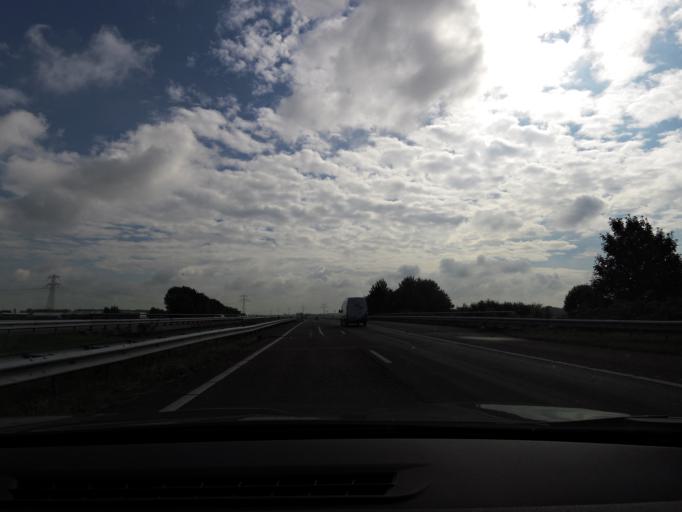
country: NL
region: Zeeland
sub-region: Gemeente Reimerswaal
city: Yerseke
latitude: 51.4202
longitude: 4.1041
